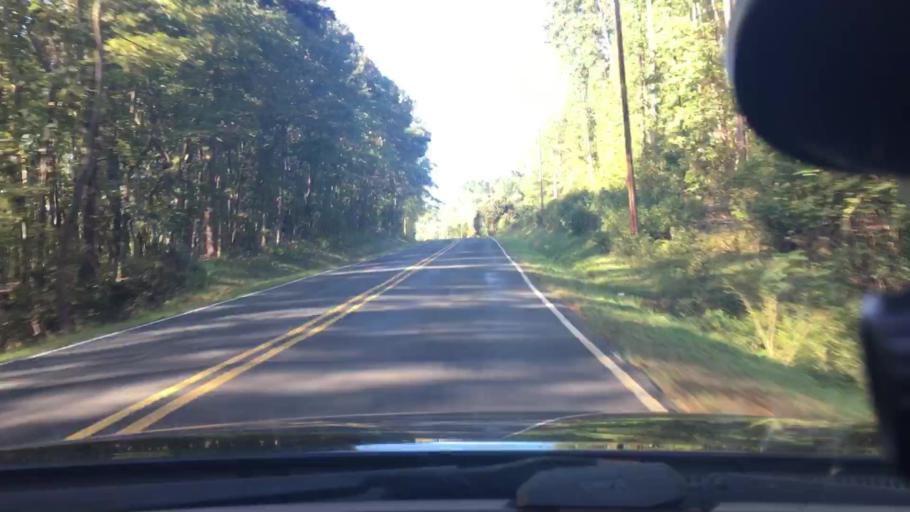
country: US
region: North Carolina
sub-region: Stanly County
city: Albemarle
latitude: 35.3325
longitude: -80.1304
